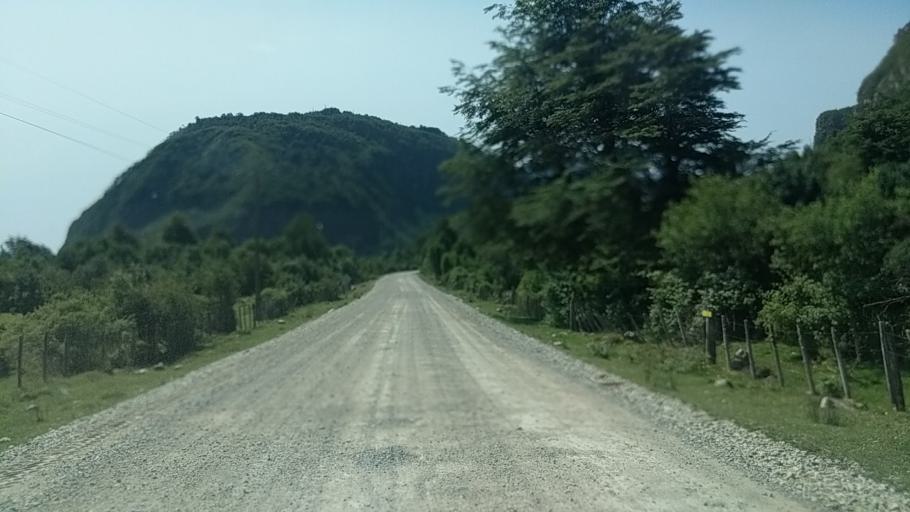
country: CL
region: Los Lagos
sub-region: Provincia de Palena
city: Palena
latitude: -43.4666
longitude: -72.1148
